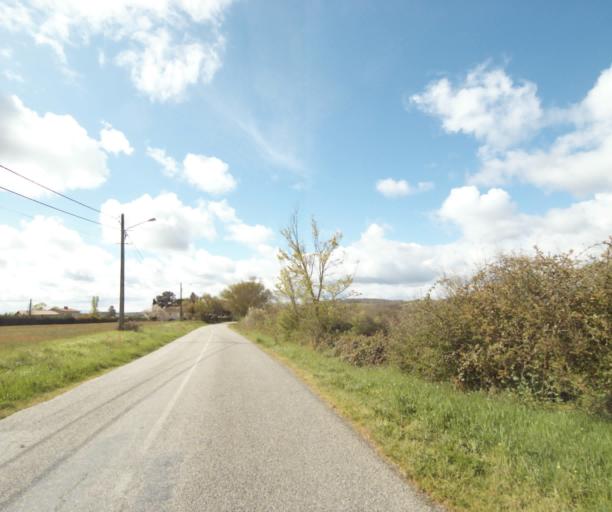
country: FR
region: Midi-Pyrenees
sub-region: Departement de l'Ariege
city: Saverdun
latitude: 43.2315
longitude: 1.5659
